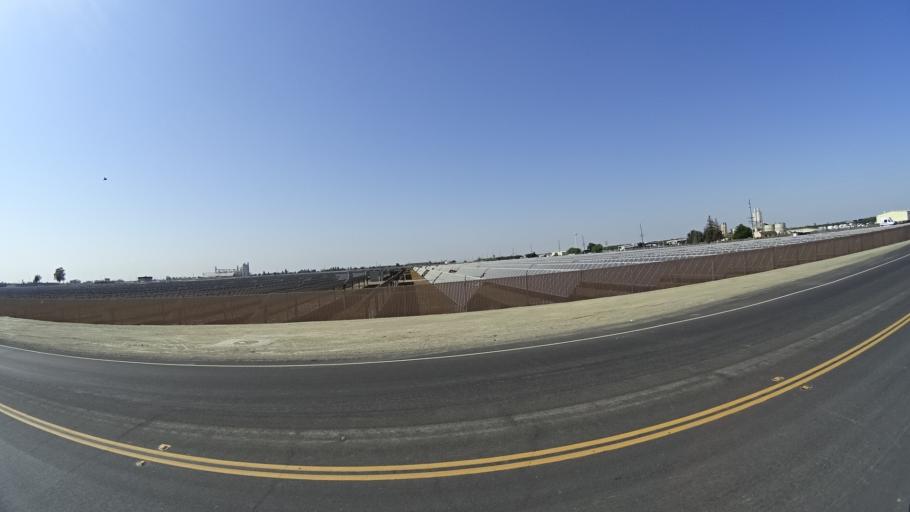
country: US
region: California
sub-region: Kings County
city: Home Garden
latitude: 36.2983
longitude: -119.6533
